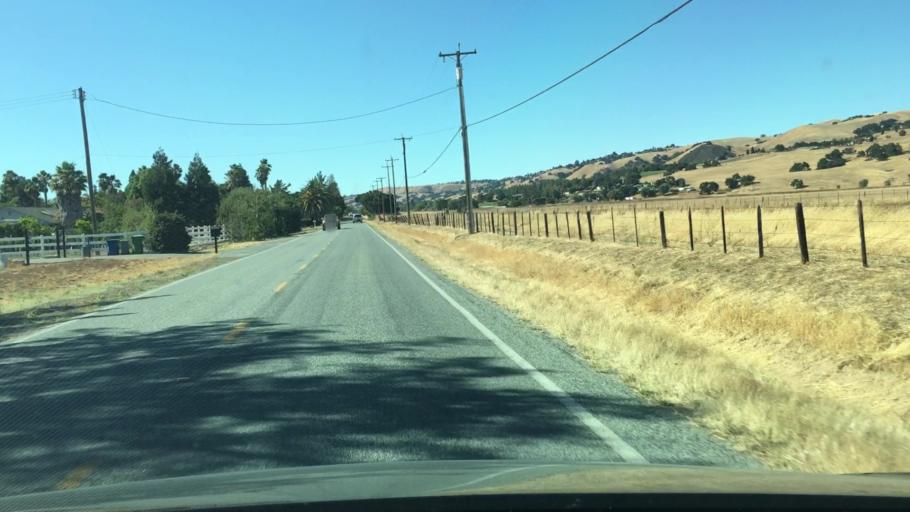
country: US
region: California
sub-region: Santa Clara County
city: San Martin
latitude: 37.0970
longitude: -121.5827
